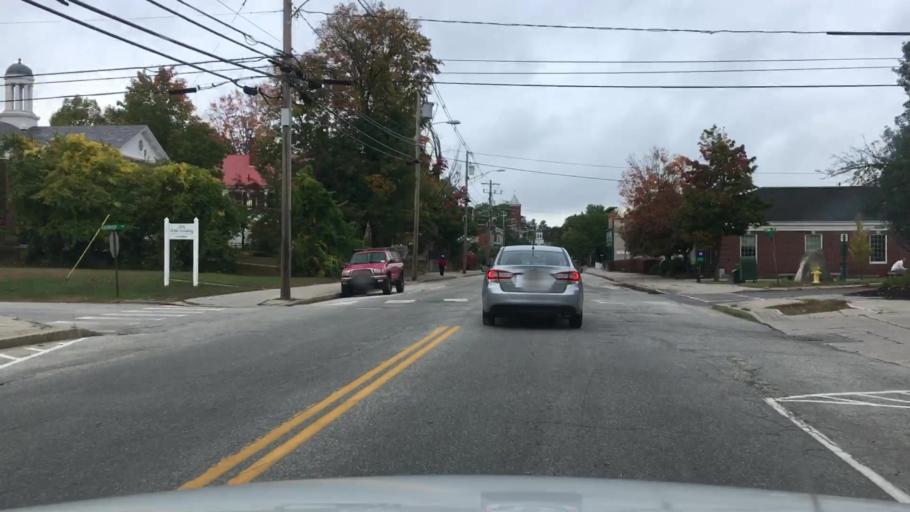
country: US
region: Maine
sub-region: Oxford County
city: Norway
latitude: 44.2125
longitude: -70.5383
